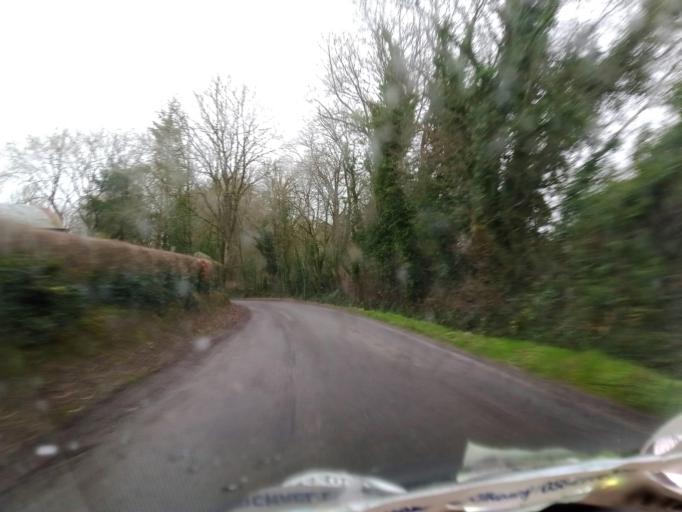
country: IE
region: Munster
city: Fethard
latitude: 52.5538
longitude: -7.7617
